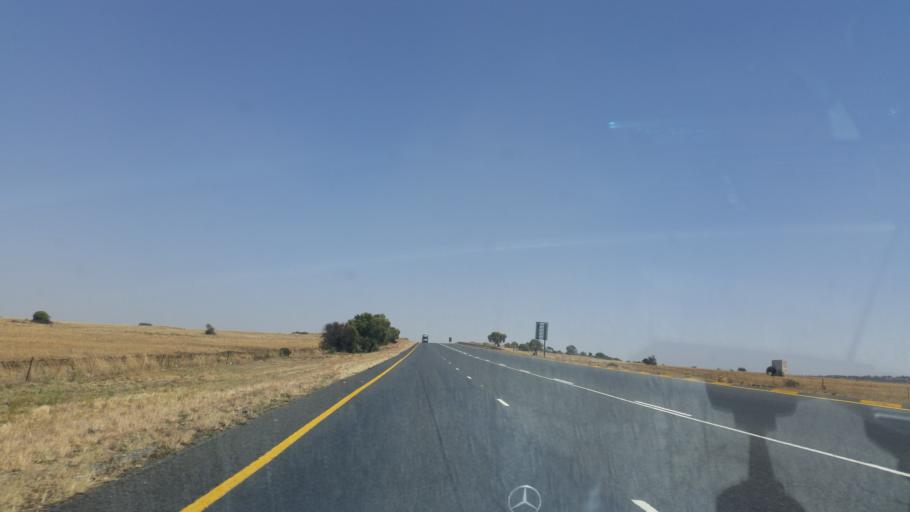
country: ZA
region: Orange Free State
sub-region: Lejweleputswa District Municipality
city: Winburg
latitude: -28.6883
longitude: 26.8181
